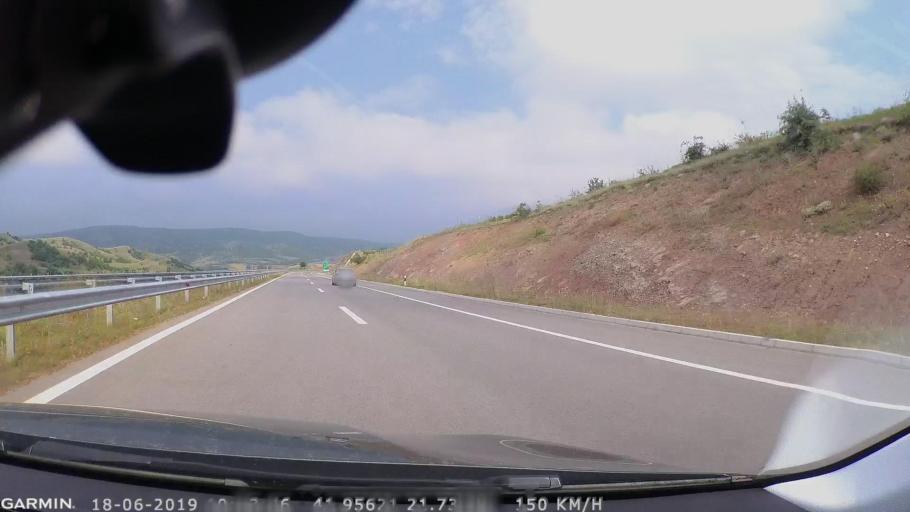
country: MK
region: Sveti Nikole
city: Gorobinci
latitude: 41.9292
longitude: 21.8289
